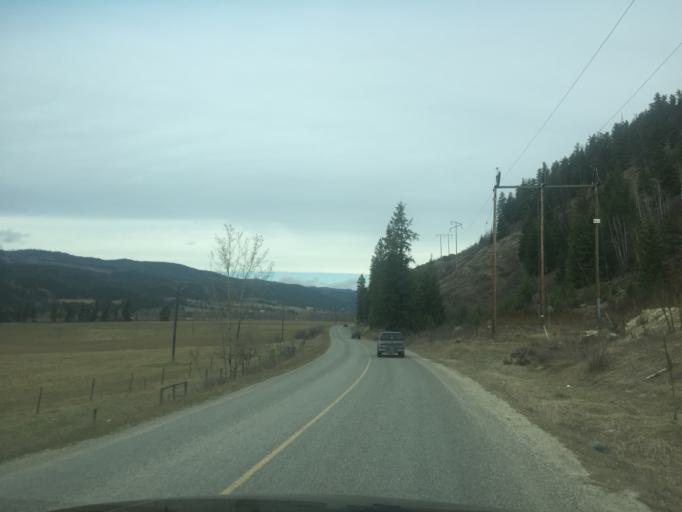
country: CA
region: British Columbia
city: Kamloops
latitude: 51.2041
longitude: -120.1369
